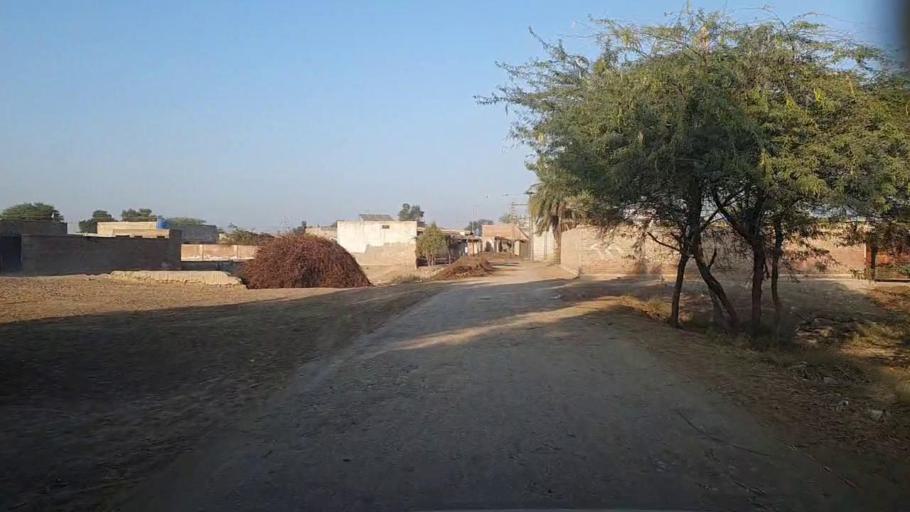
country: PK
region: Sindh
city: Khairpur
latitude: 28.0754
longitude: 69.7455
